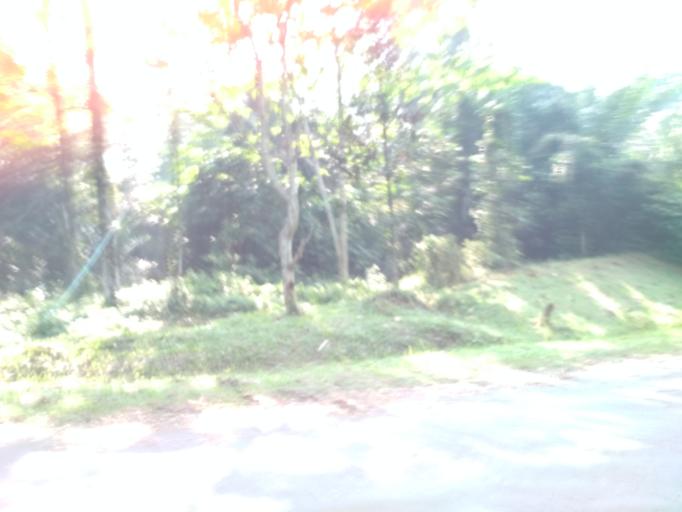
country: ID
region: West Java
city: Ciampea
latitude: -6.5582
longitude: 106.7199
